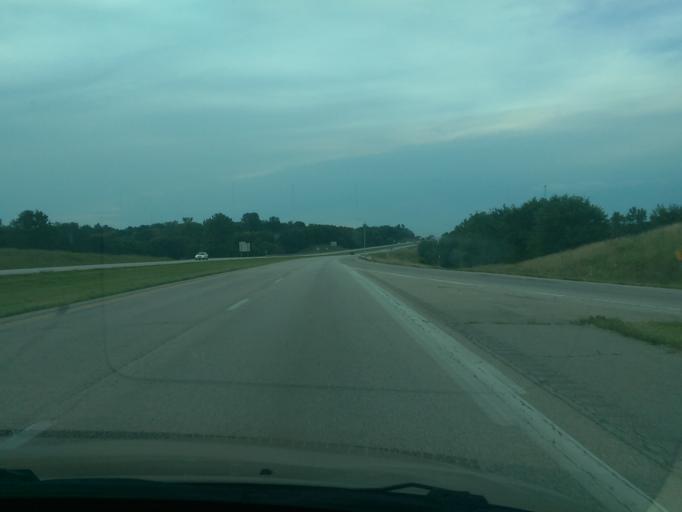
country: US
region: Missouri
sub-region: Andrew County
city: Country Club Village
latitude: 39.8175
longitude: -94.8043
